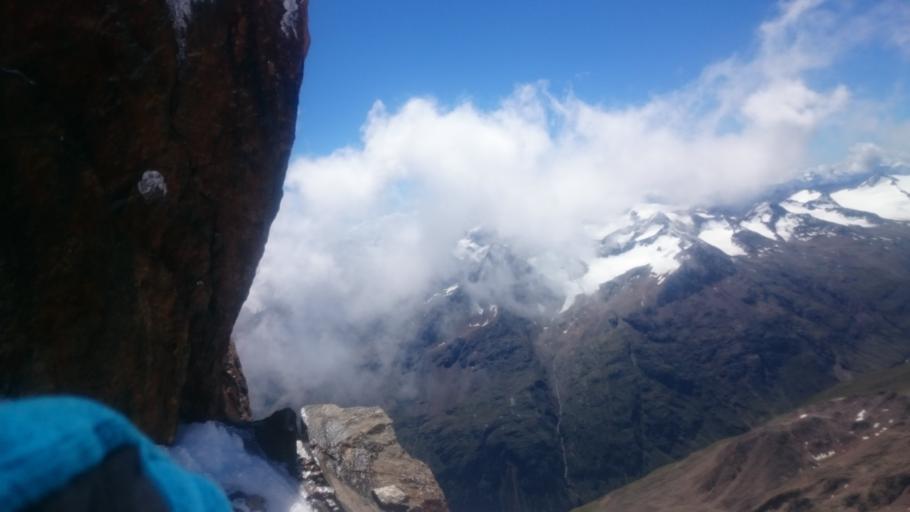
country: AT
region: Tyrol
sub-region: Politischer Bezirk Imst
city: Soelden
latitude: 46.8851
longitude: 10.8670
